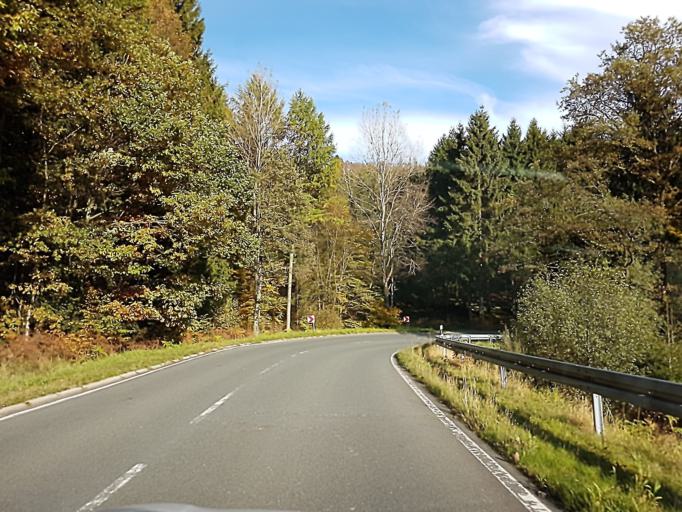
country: DE
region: North Rhine-Westphalia
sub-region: Regierungsbezirk Arnsberg
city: Drolshagen
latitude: 51.1010
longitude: 7.7746
